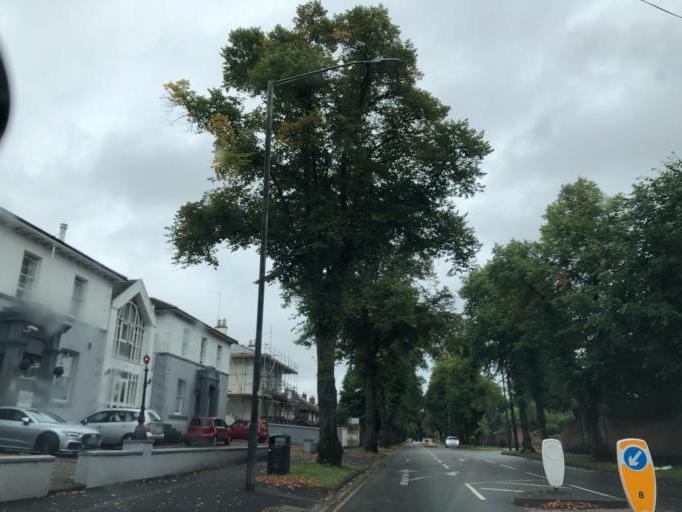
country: GB
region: England
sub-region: Warwickshire
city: Royal Leamington Spa
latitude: 52.2898
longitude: -1.5496
